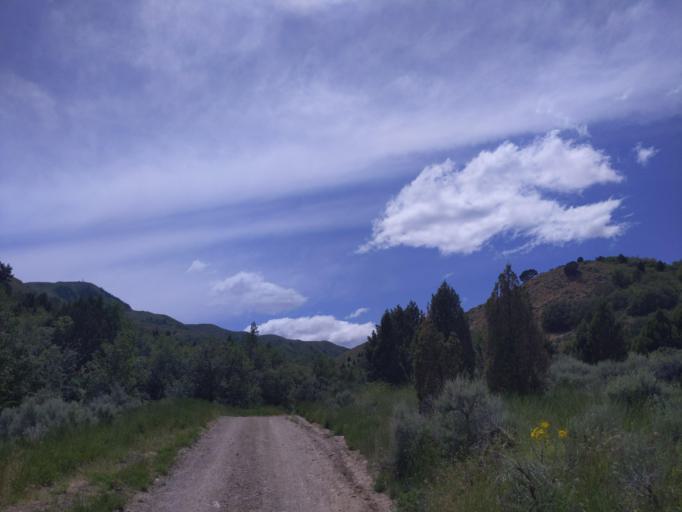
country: US
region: Idaho
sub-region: Bannock County
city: Pocatello
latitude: 42.8328
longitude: -112.4775
